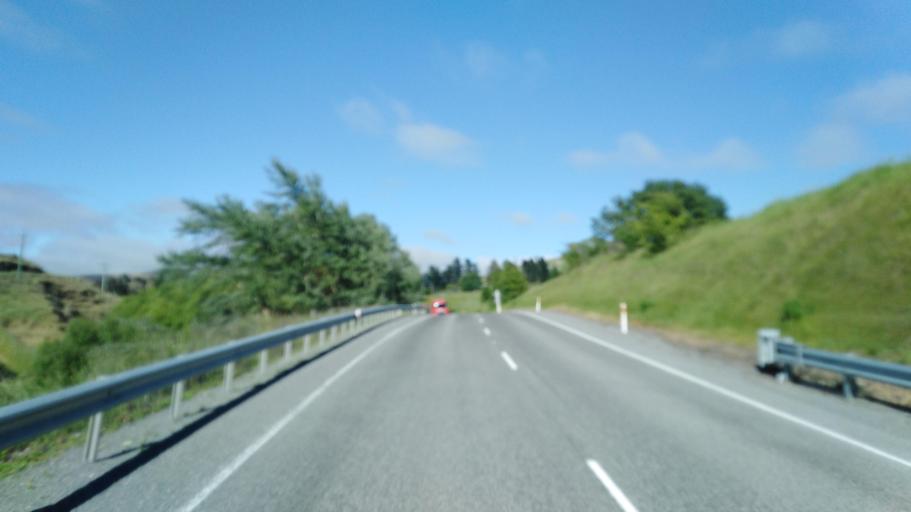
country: NZ
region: Canterbury
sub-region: Hurunui District
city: Amberley
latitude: -43.0049
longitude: 172.7073
